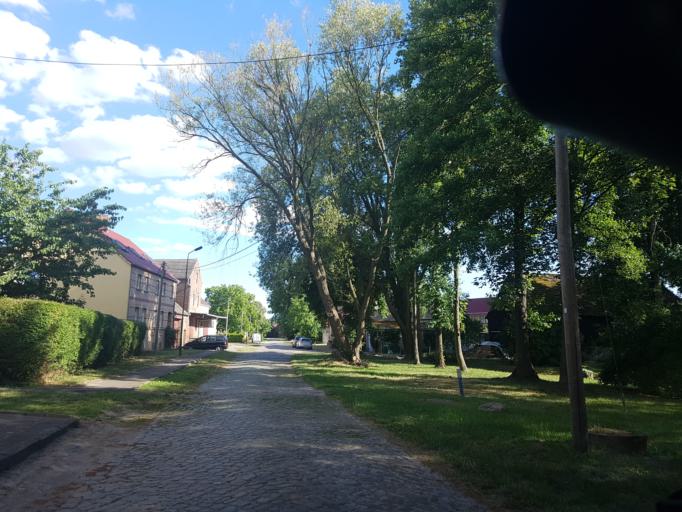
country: DE
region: Brandenburg
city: Juterbog
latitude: 51.9267
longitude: 13.1408
